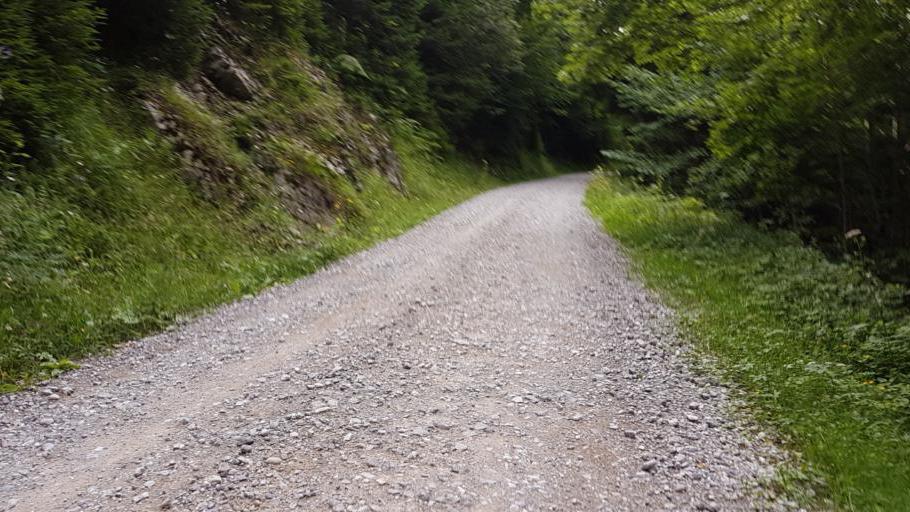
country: CH
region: Bern
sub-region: Obersimmental-Saanen District
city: Boltigen
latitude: 46.6788
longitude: 7.4517
